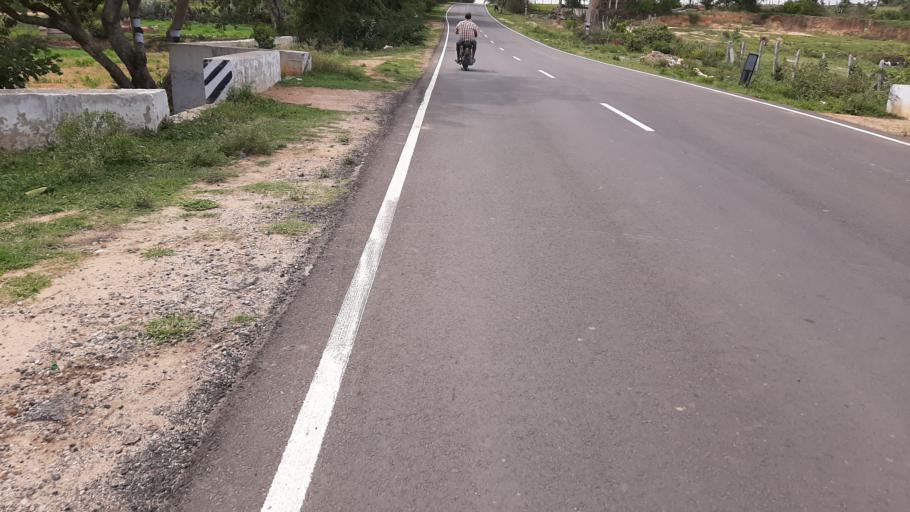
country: IN
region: Tamil Nadu
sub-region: Krishnagiri
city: Denkanikota
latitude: 12.5333
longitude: 77.7780
